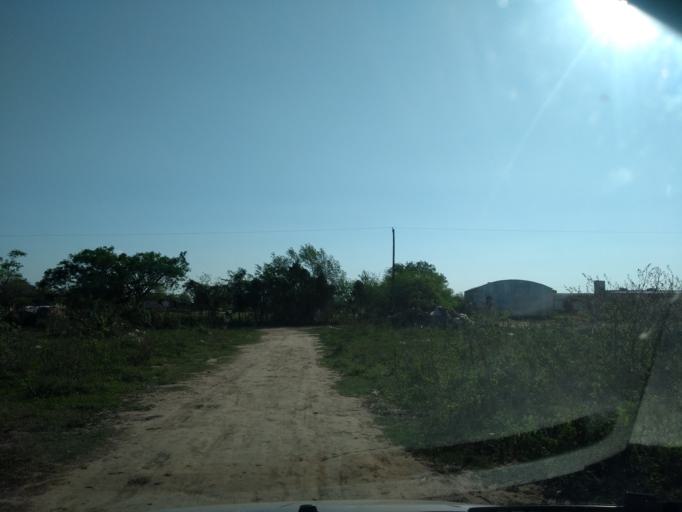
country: AR
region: Chaco
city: Fontana
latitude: -27.4123
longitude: -59.0123
